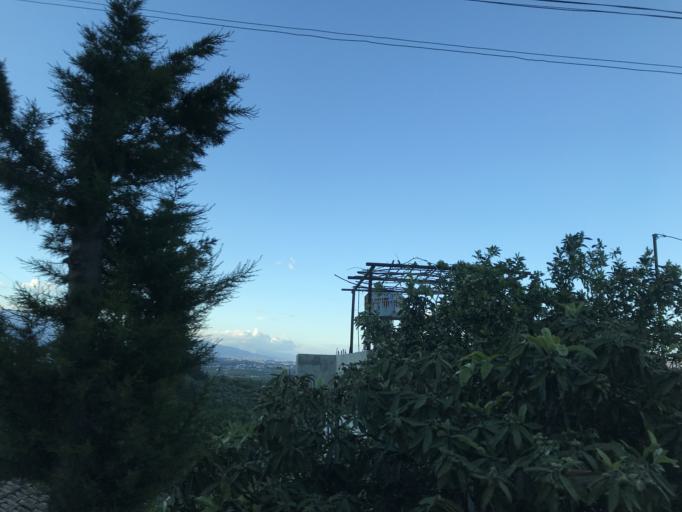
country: TR
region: Hatay
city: Buyukcat
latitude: 36.1002
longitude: 36.0551
